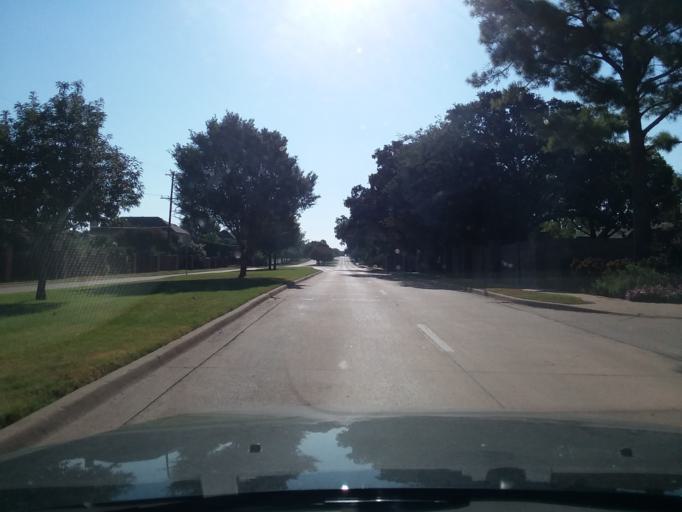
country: US
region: Texas
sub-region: Denton County
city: Highland Village
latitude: 33.0497
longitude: -97.0522
